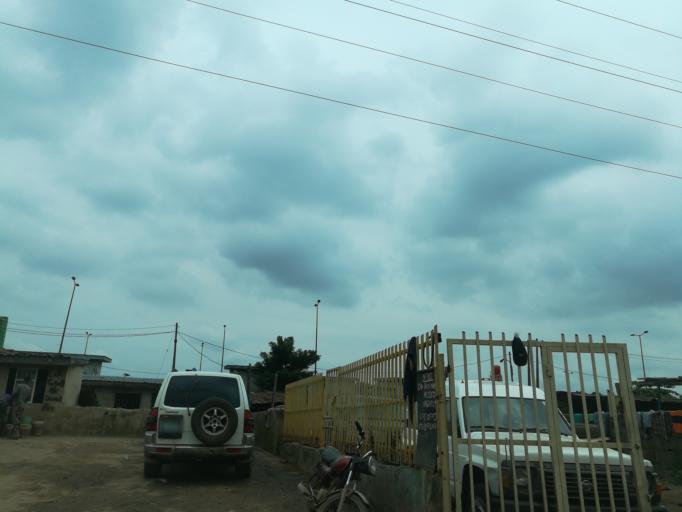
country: NG
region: Lagos
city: Ojota
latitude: 6.6111
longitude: 3.4140
